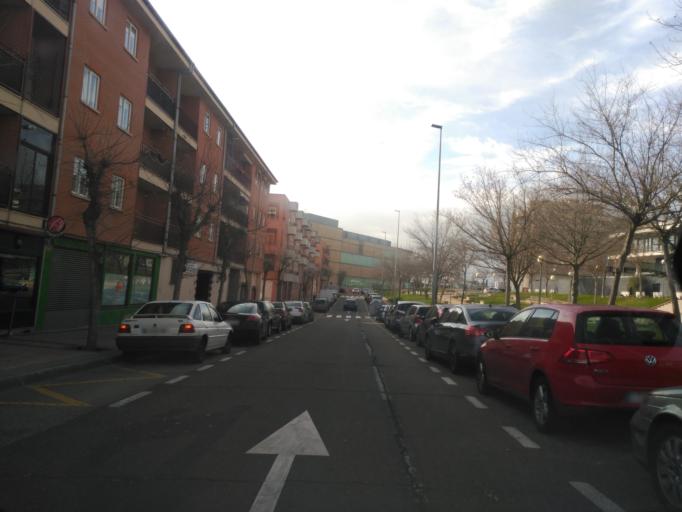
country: ES
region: Castille and Leon
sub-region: Provincia de Salamanca
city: Salamanca
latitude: 40.9616
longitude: -5.6503
